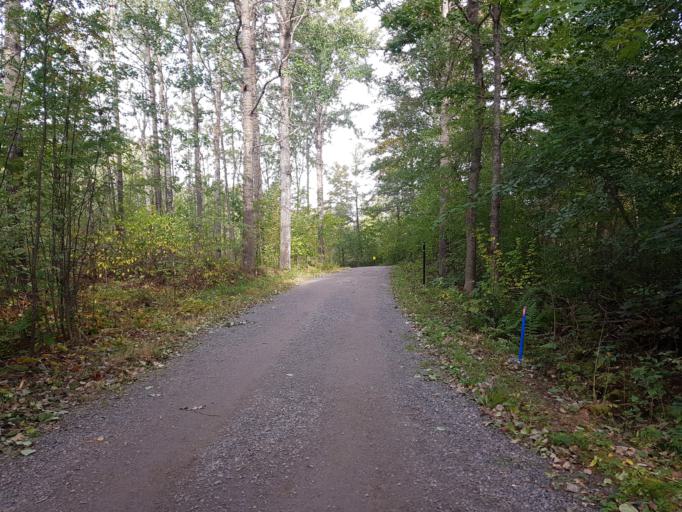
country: FI
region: Uusimaa
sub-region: Helsinki
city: Helsinki
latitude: 60.1363
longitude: 25.0058
